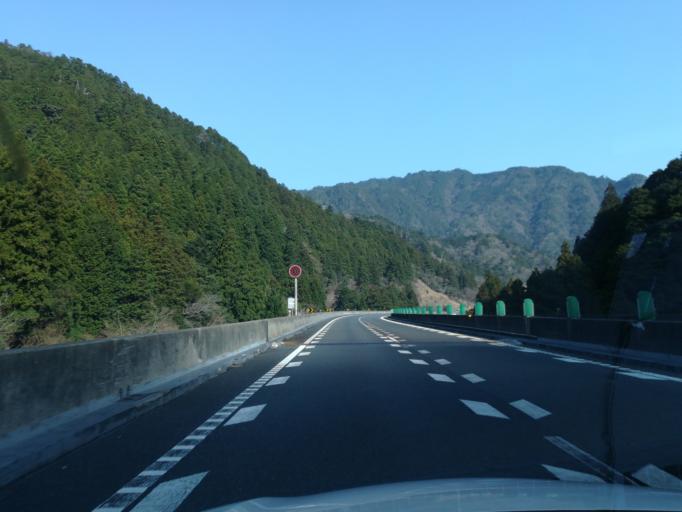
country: JP
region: Ehime
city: Kawanoecho
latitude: 33.9060
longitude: 133.6306
